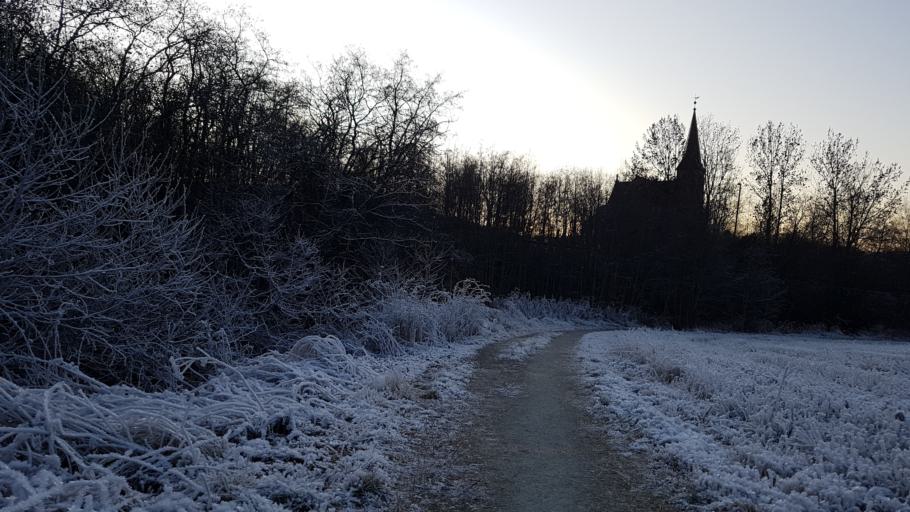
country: NO
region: Sor-Trondelag
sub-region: Melhus
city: Melhus
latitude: 63.2741
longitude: 10.2965
